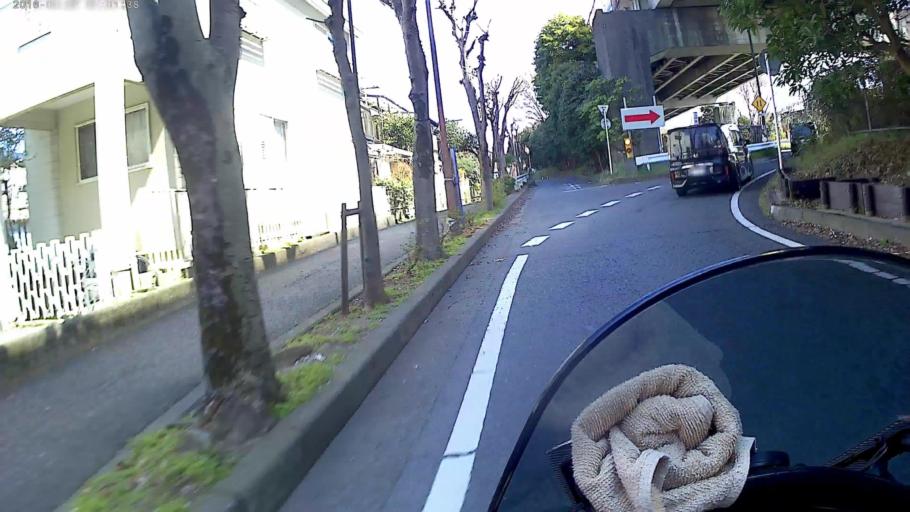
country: JP
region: Kanagawa
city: Chigasaki
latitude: 35.3474
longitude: 139.4261
